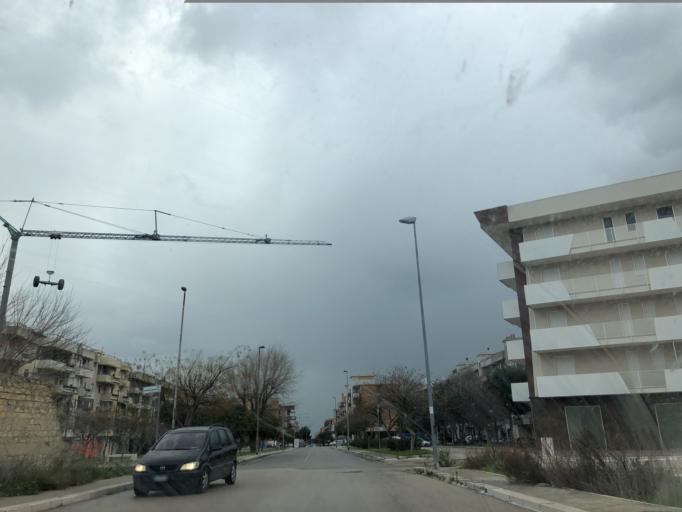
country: IT
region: Apulia
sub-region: Provincia di Foggia
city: Lucera
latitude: 41.5022
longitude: 15.3438
